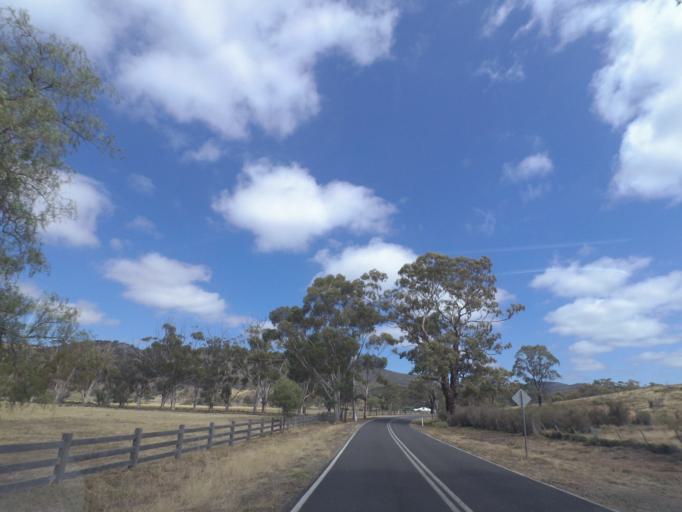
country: AU
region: Victoria
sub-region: Moorabool
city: Bacchus Marsh
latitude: -37.6309
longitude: 144.4308
